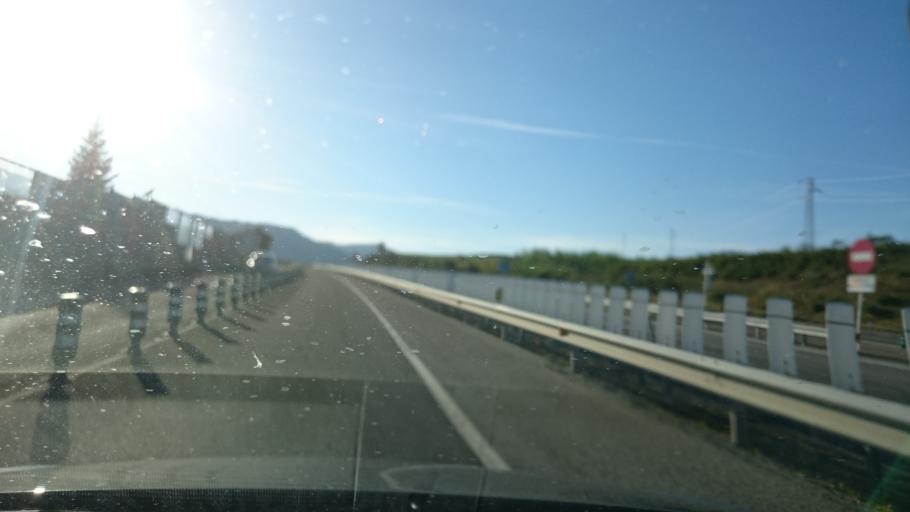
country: ES
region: Castille and Leon
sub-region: Provincia de Leon
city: Villadecanes
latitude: 42.5753
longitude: -6.7743
